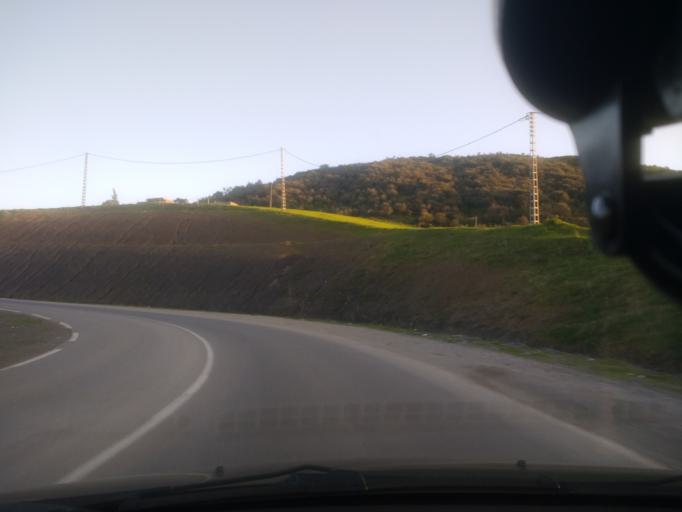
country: DZ
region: Boumerdes
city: Makouda
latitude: 36.7563
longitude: 4.0503
